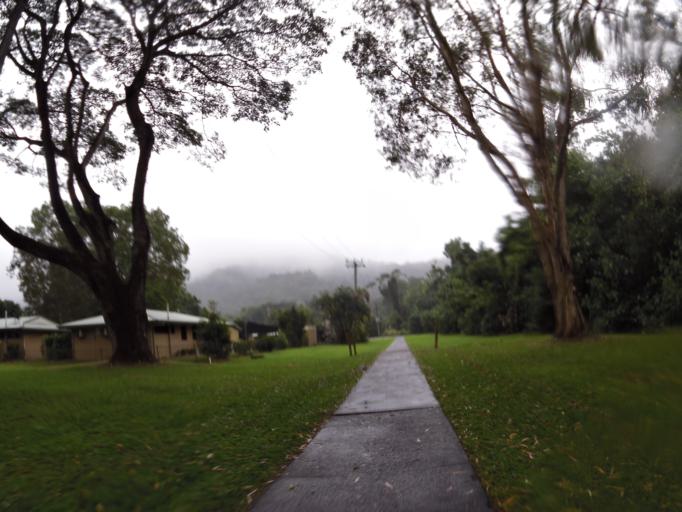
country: AU
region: Queensland
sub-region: Cairns
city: Cairns
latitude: -16.9029
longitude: 145.7462
